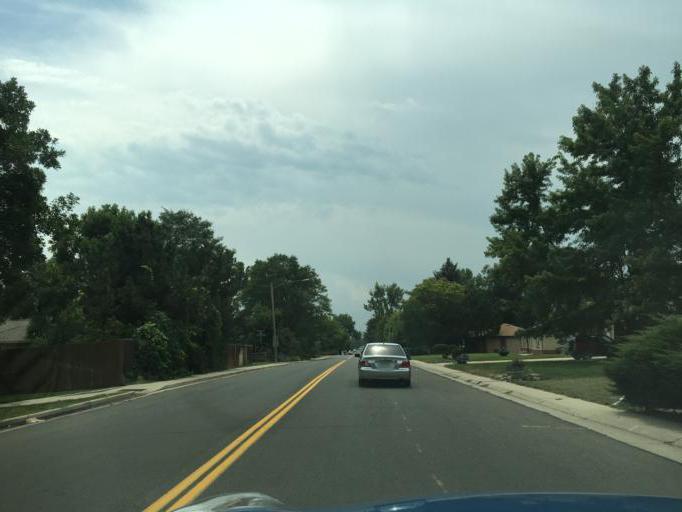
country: US
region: Colorado
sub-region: Jefferson County
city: Wheat Ridge
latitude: 39.7461
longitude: -105.0908
